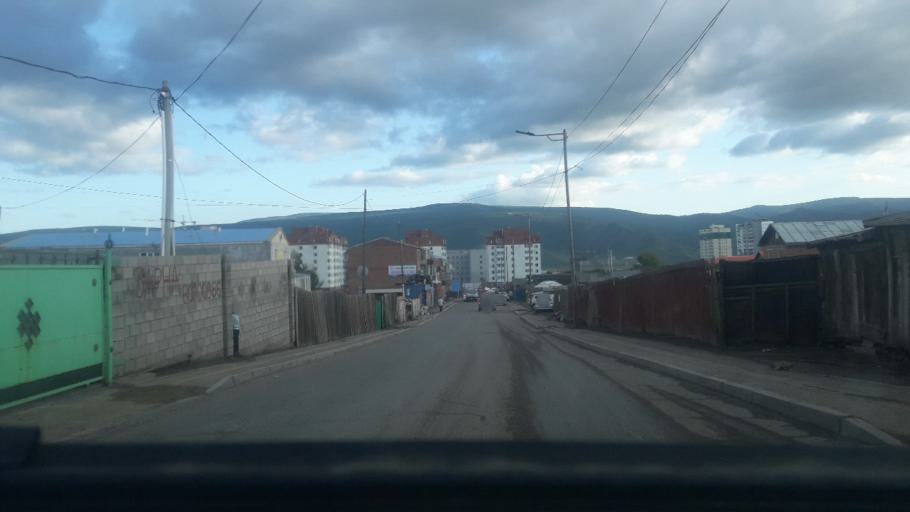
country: MN
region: Ulaanbaatar
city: Ulaanbaatar
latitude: 47.9204
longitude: 106.9955
